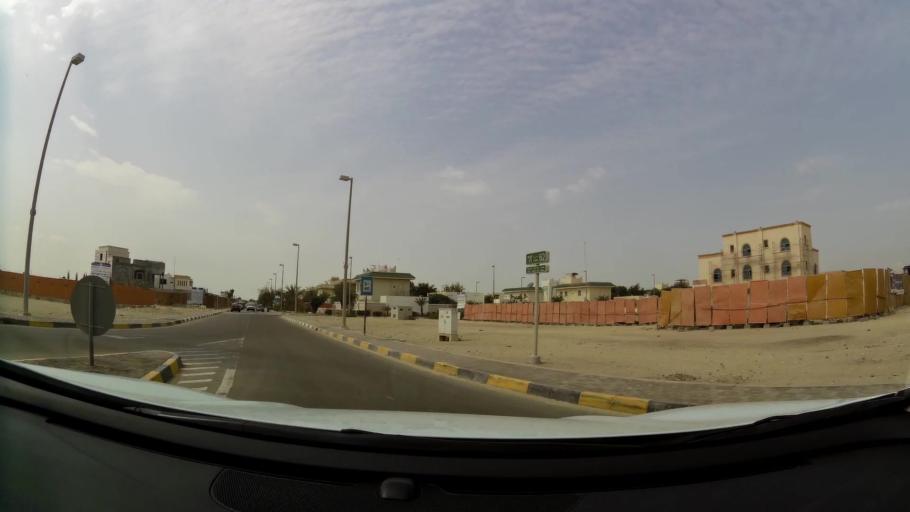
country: AE
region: Abu Dhabi
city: Abu Dhabi
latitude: 24.5255
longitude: 54.6903
